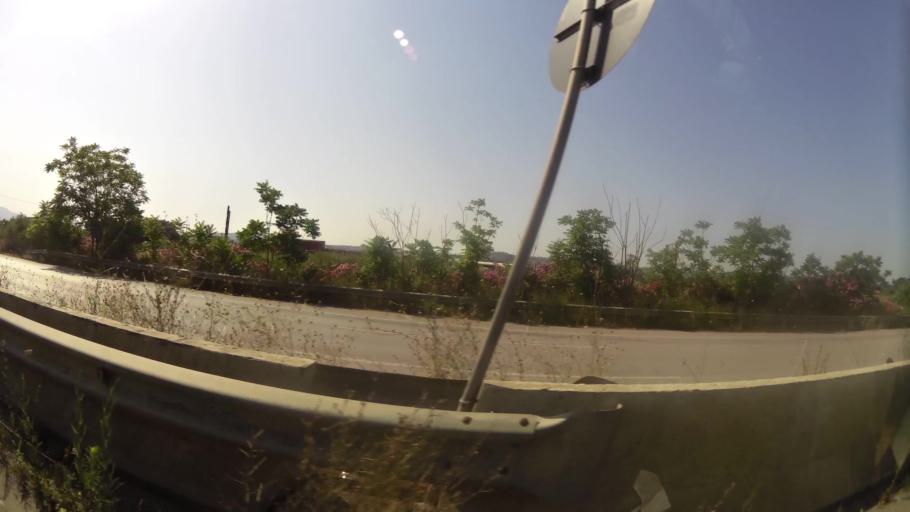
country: GR
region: Central Macedonia
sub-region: Nomos Thessalonikis
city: Neo Rysi
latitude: 40.5119
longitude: 22.9836
